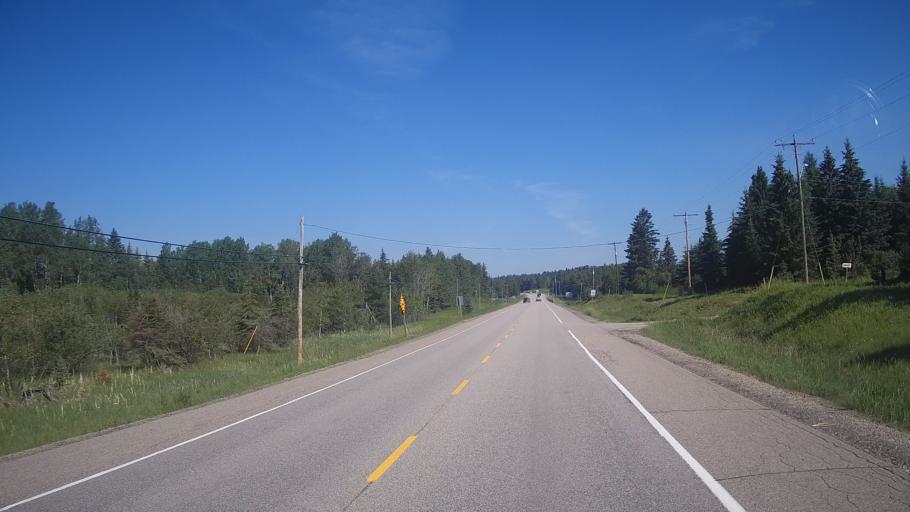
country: CA
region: Ontario
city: Dryden
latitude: 49.7772
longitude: -92.6954
